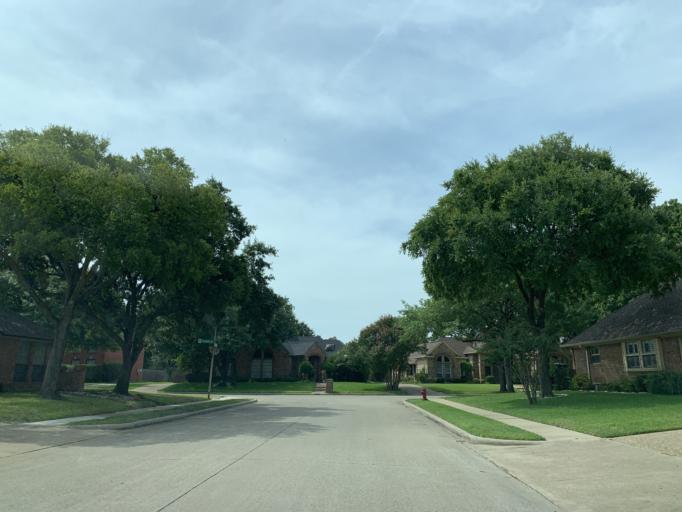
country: US
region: Texas
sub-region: Dallas County
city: Grand Prairie
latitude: 32.6687
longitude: -97.0014
